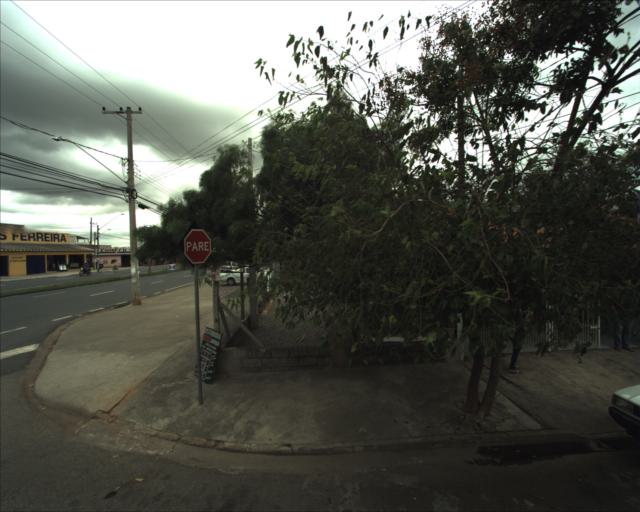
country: BR
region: Sao Paulo
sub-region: Sorocaba
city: Sorocaba
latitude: -23.4362
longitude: -47.5060
